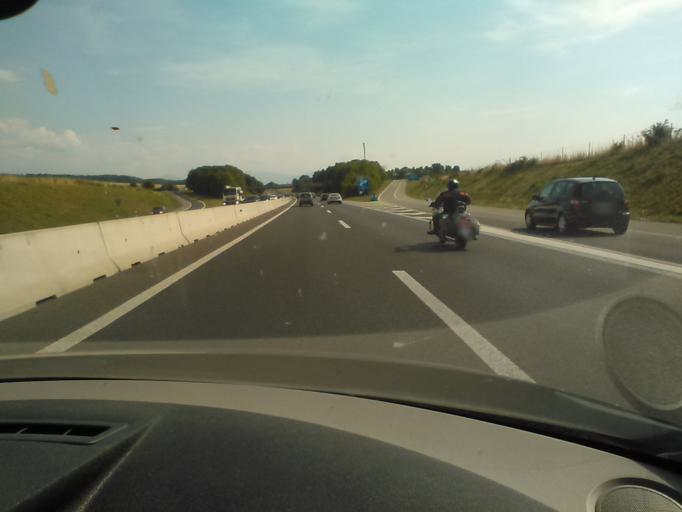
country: CH
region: Vaud
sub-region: Gros-de-Vaud District
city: Penthalaz
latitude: 46.6011
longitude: 6.5537
